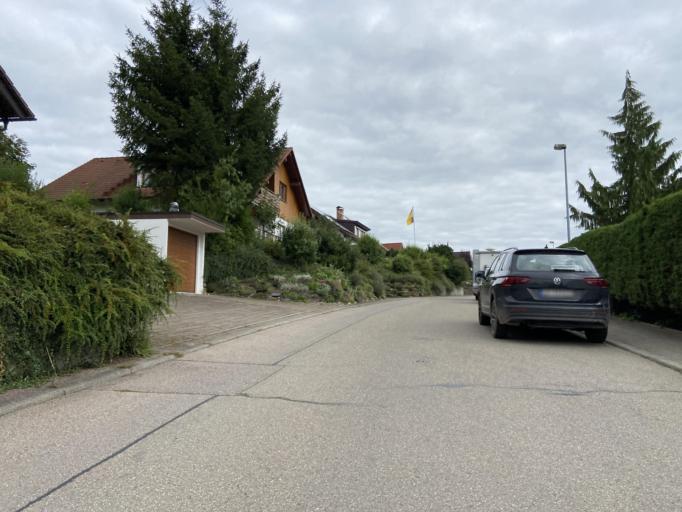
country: DE
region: Baden-Wuerttemberg
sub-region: Tuebingen Region
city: Sigmaringendorf
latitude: 48.0729
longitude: 9.2581
